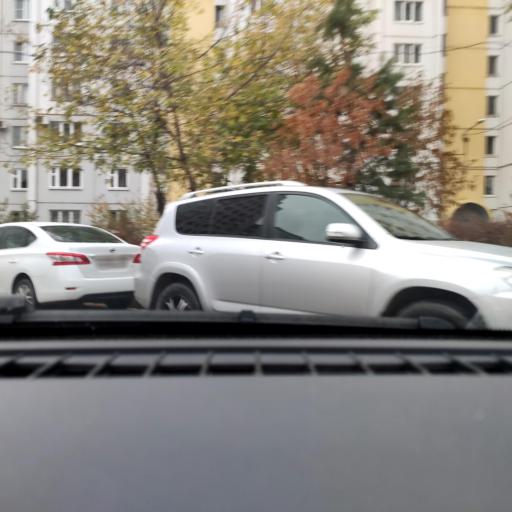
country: RU
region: Voronezj
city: Somovo
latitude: 51.6904
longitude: 39.2819
